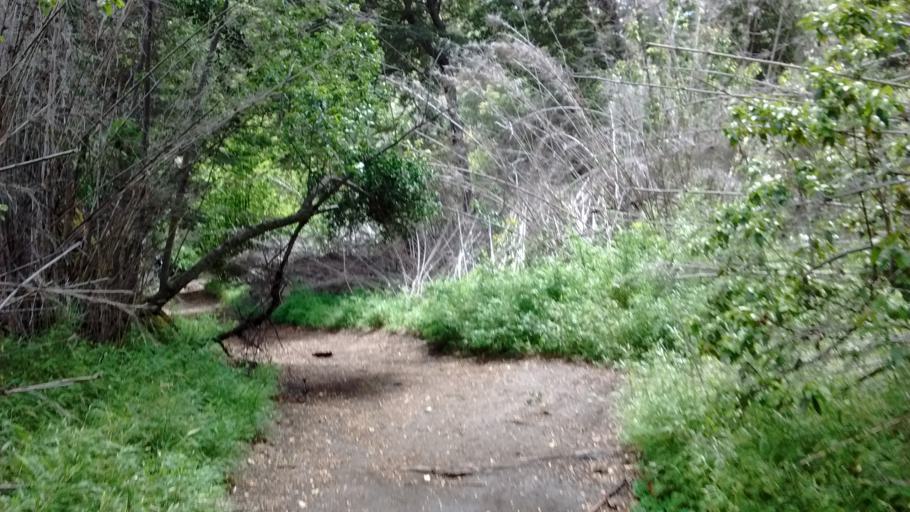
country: AR
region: Rio Negro
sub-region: Departamento de Bariloche
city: San Carlos de Bariloche
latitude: -41.0580
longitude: -71.5654
